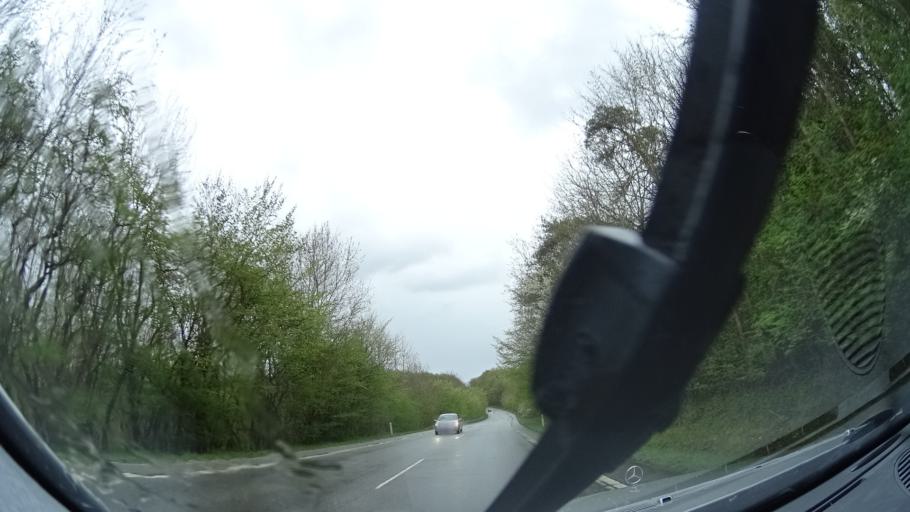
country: DK
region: Zealand
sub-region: Lejre Kommune
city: Ejby
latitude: 55.6898
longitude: 11.7924
